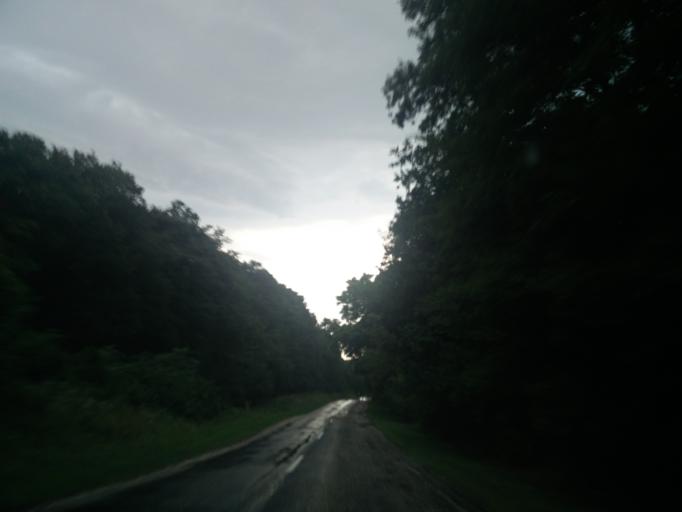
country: HU
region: Fejer
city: Pazmand
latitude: 47.2670
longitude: 18.5983
